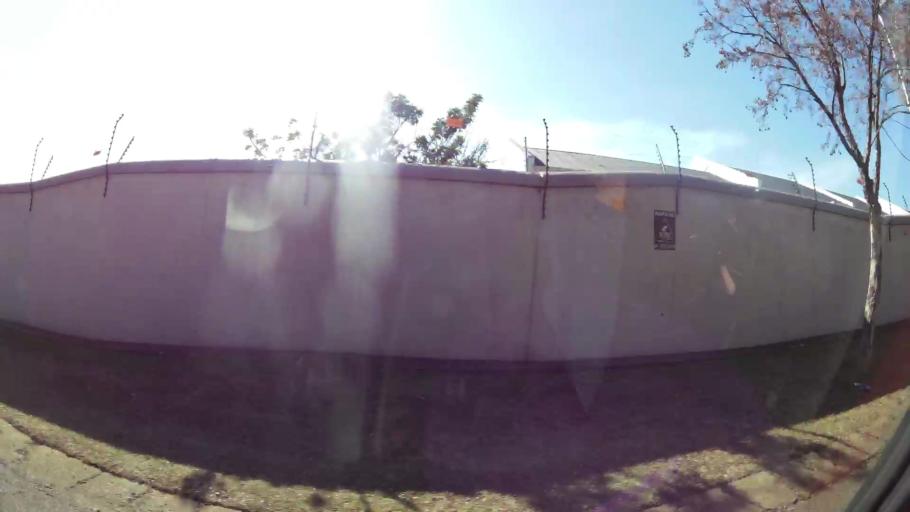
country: ZA
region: Gauteng
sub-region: City of Johannesburg Metropolitan Municipality
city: Roodepoort
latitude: -26.1193
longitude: 27.9616
